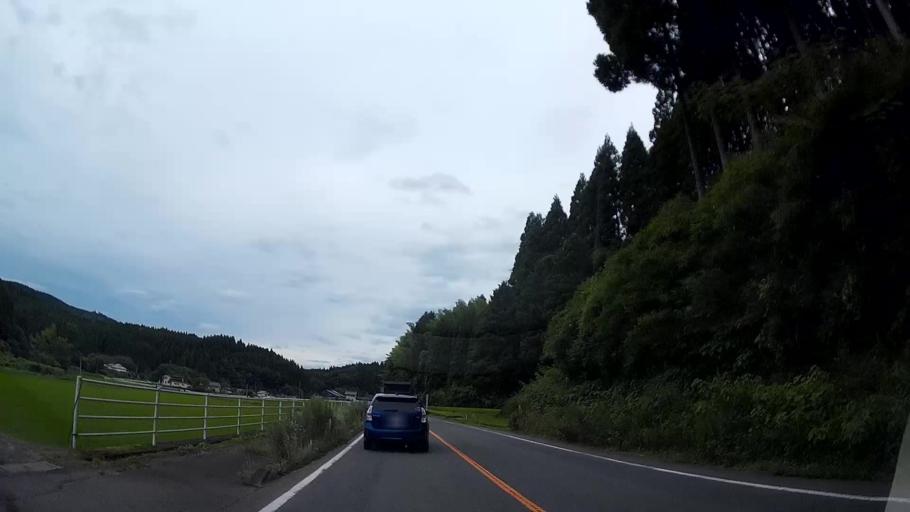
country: JP
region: Kumamoto
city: Aso
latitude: 33.1259
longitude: 131.0324
